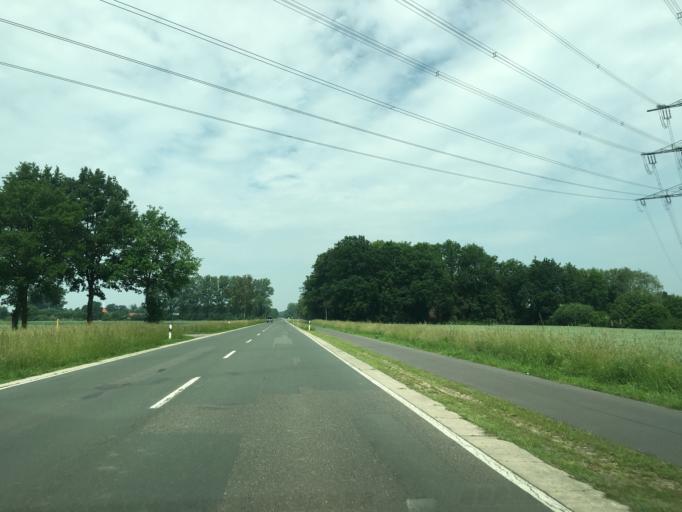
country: DE
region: North Rhine-Westphalia
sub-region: Regierungsbezirk Munster
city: Altenberge
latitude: 52.0793
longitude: 7.4300
